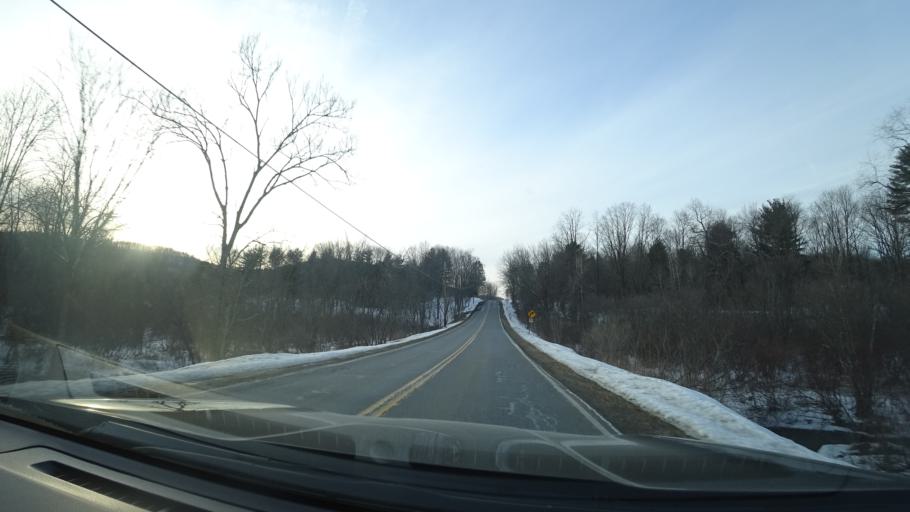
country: US
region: New York
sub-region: Washington County
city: Cambridge
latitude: 43.1755
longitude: -73.3612
